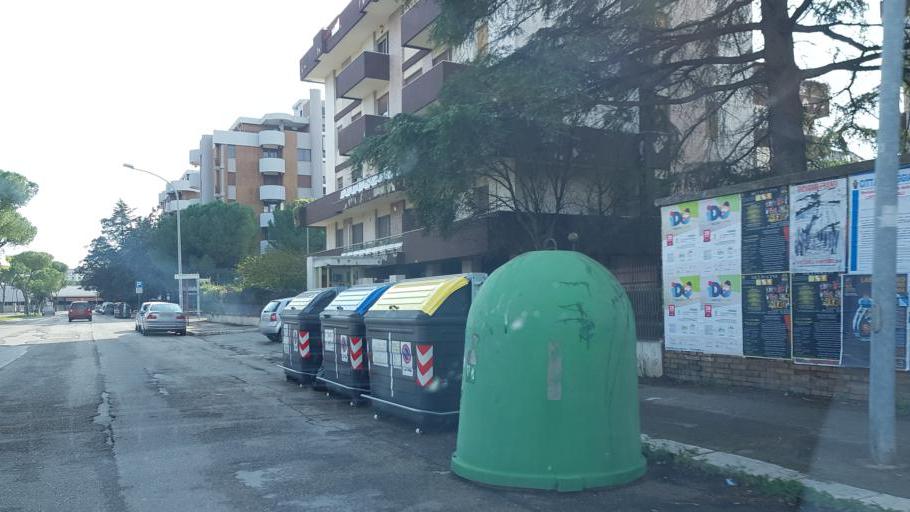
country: IT
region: Apulia
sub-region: Provincia di Foggia
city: Foggia
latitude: 41.4563
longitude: 15.5617
